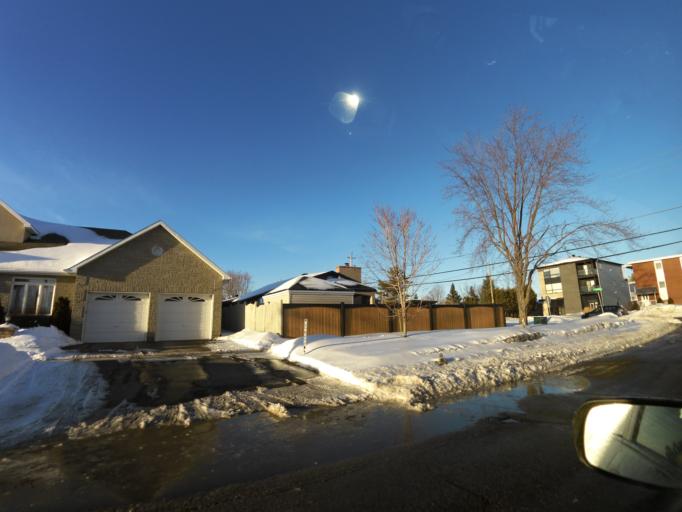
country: CA
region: Ontario
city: Ottawa
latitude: 45.4428
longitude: -75.5257
